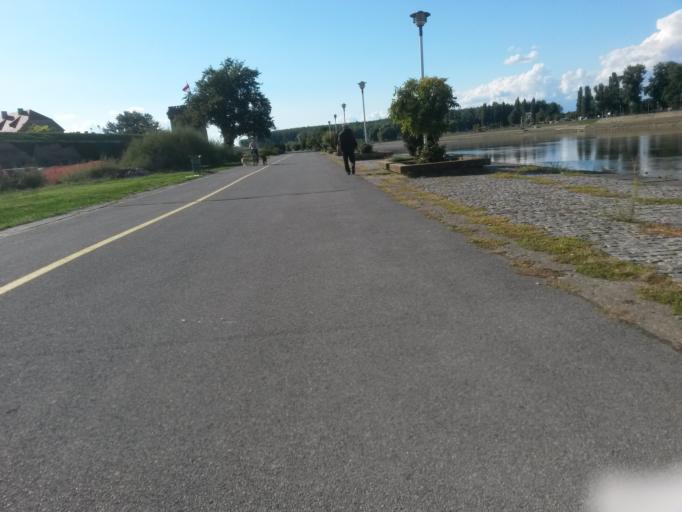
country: HR
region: Osjecko-Baranjska
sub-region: Grad Osijek
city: Osijek
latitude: 45.5620
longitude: 18.6991
